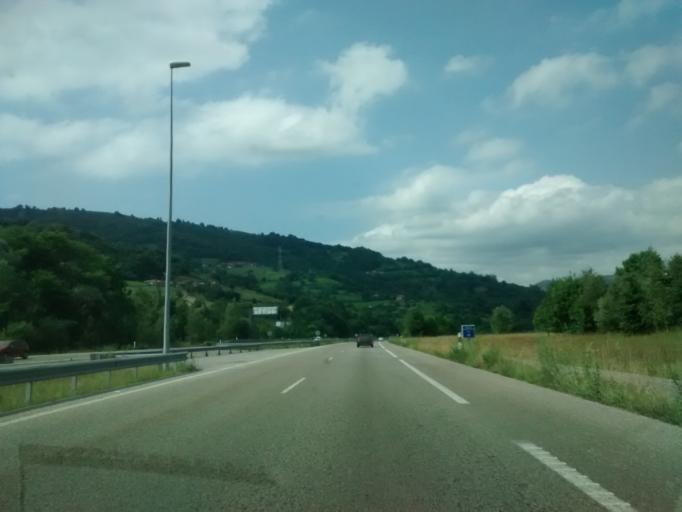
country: ES
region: Asturias
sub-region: Province of Asturias
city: Mieres
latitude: 43.2898
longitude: -5.7568
